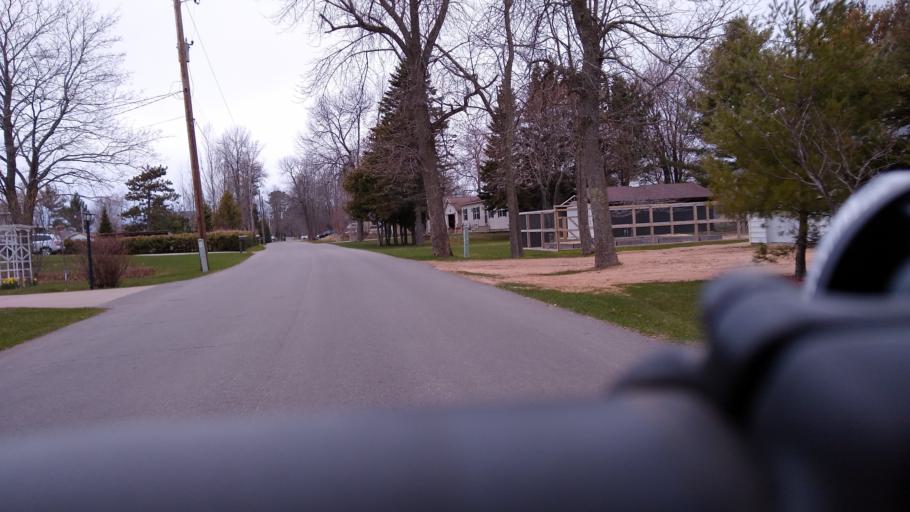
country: US
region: Michigan
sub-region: Delta County
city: Escanaba
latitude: 45.7043
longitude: -87.0858
